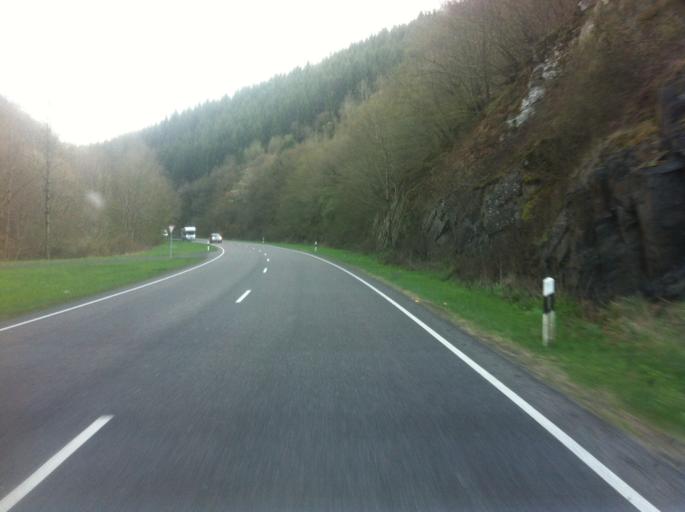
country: LU
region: Diekirch
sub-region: Canton de Wiltz
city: Esch-sur-Sure
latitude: 49.9224
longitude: 5.9420
